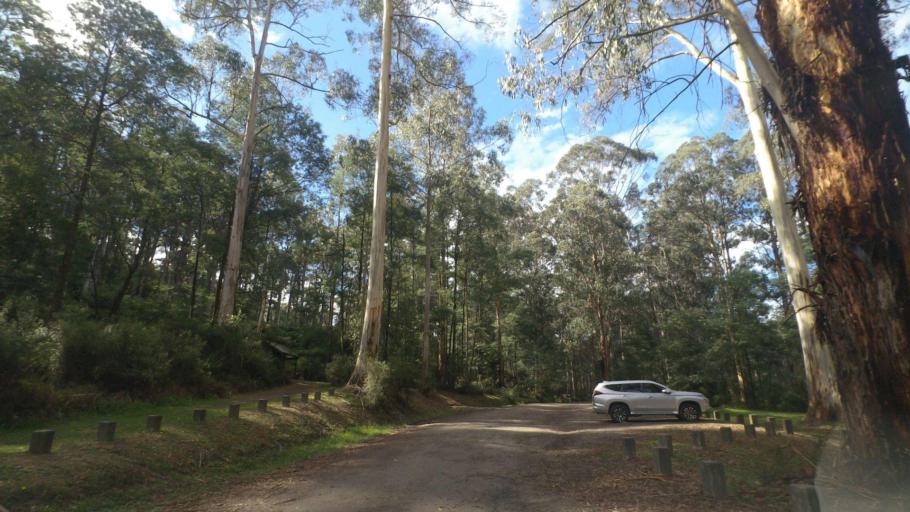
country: AU
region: Victoria
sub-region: Cardinia
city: Gembrook
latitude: -37.9841
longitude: 145.5954
